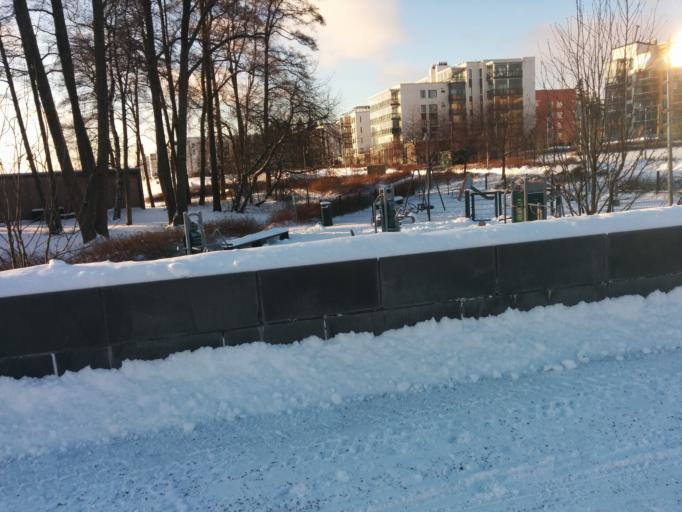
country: FI
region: Uusimaa
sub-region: Helsinki
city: Vantaa
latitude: 60.2027
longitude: 25.1613
